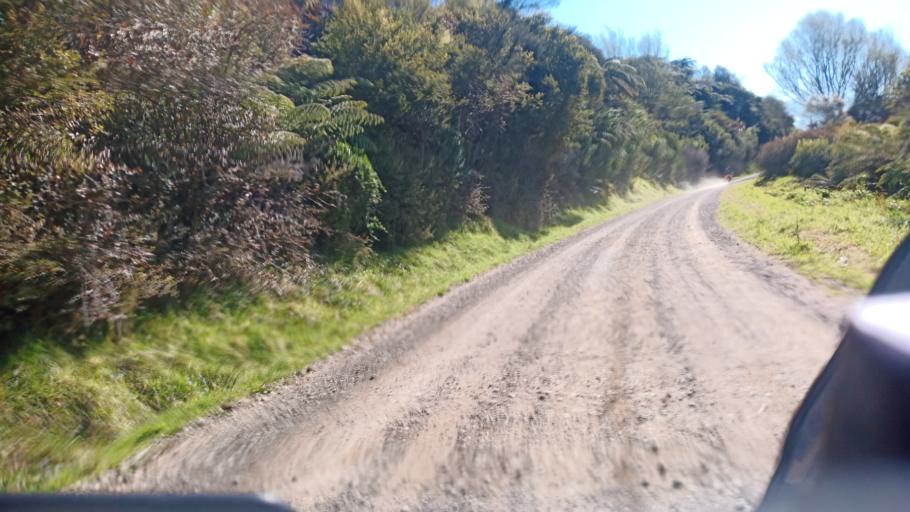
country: NZ
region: Bay of Plenty
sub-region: Opotiki District
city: Opotiki
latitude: -38.0178
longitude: 177.4303
